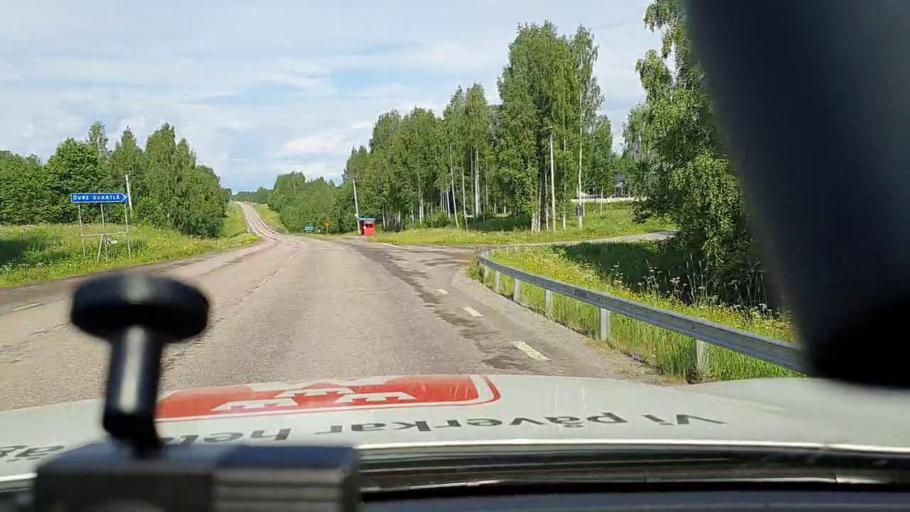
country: SE
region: Norrbotten
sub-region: Alvsbyns Kommun
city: AElvsbyn
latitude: 66.0126
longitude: 21.1718
